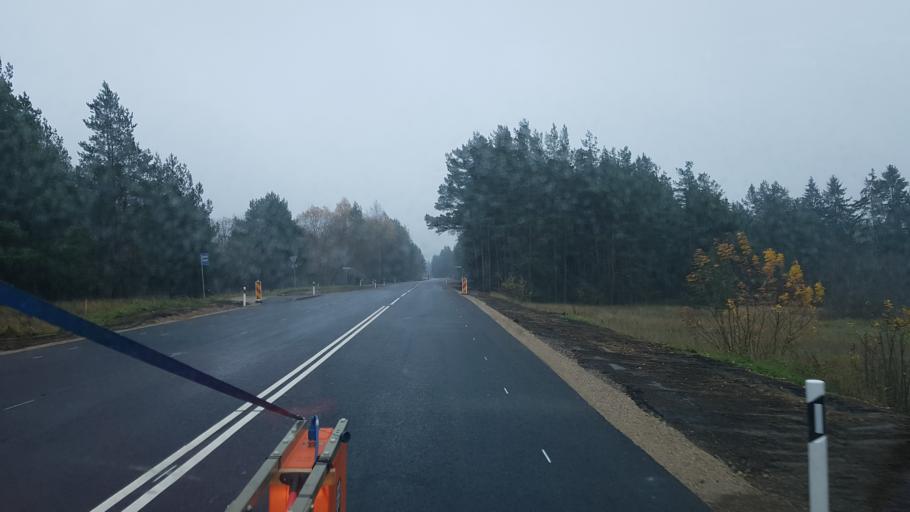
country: EE
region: Raplamaa
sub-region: Kohila vald
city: Kohila
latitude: 59.1810
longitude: 24.7819
